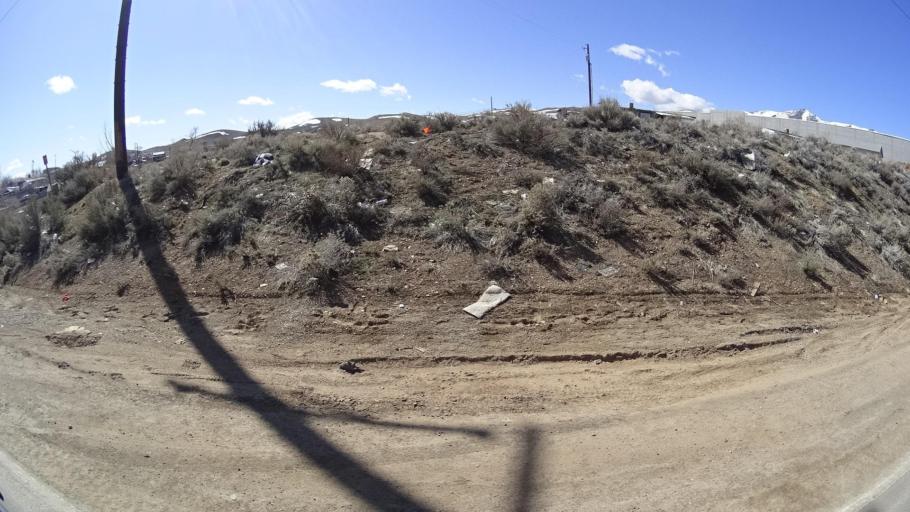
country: US
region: Nevada
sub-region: Washoe County
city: Golden Valley
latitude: 39.6058
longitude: -119.8581
